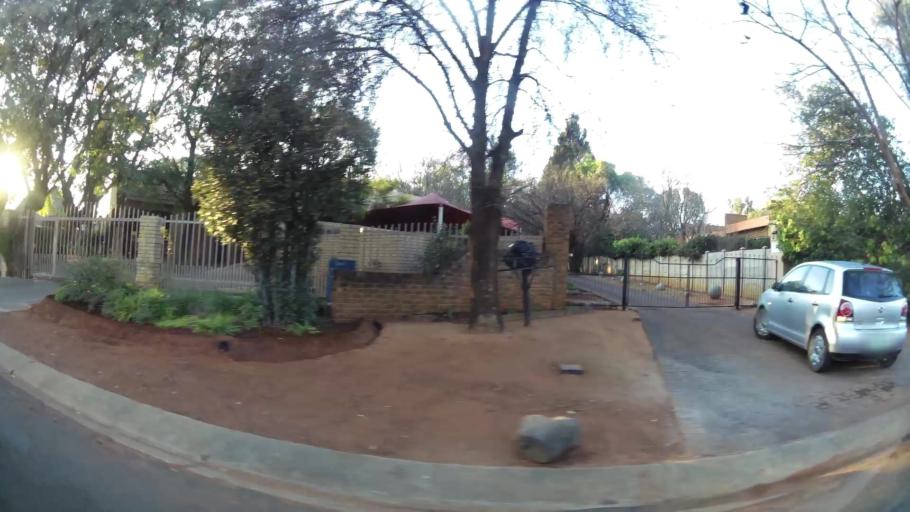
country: ZA
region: Orange Free State
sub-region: Mangaung Metropolitan Municipality
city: Bloemfontein
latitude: -29.0914
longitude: 26.1534
